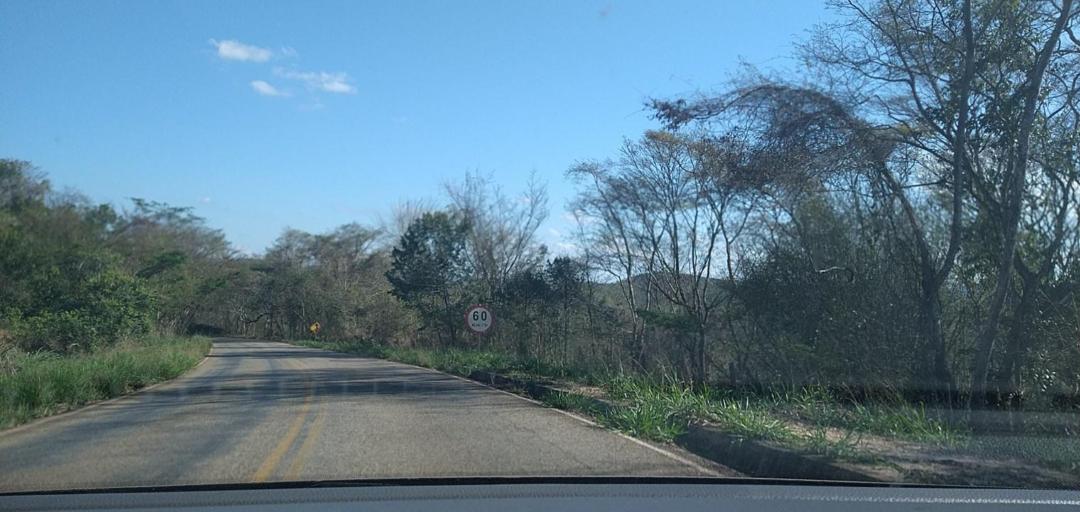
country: BR
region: Minas Gerais
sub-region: Ponte Nova
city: Ponte Nova
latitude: -20.2334
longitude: -42.9017
